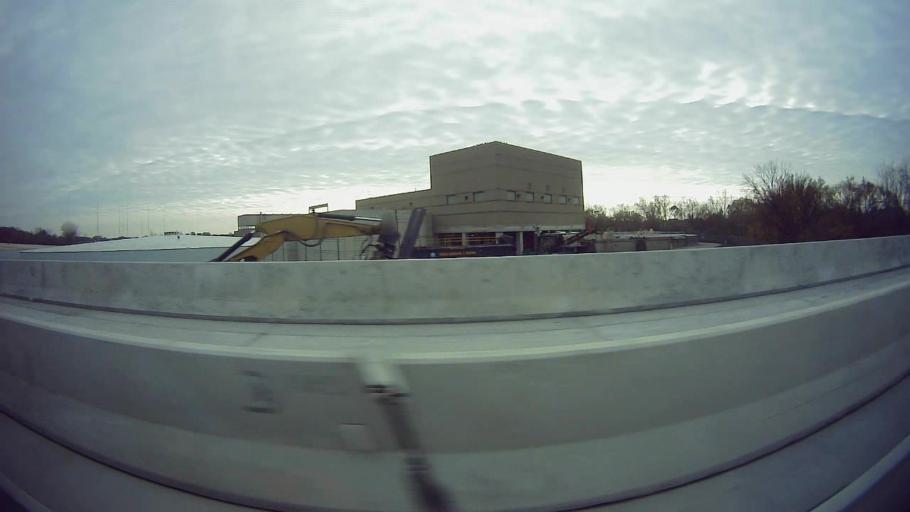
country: US
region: Michigan
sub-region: Wayne County
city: Southgate
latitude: 42.2308
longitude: -83.2093
